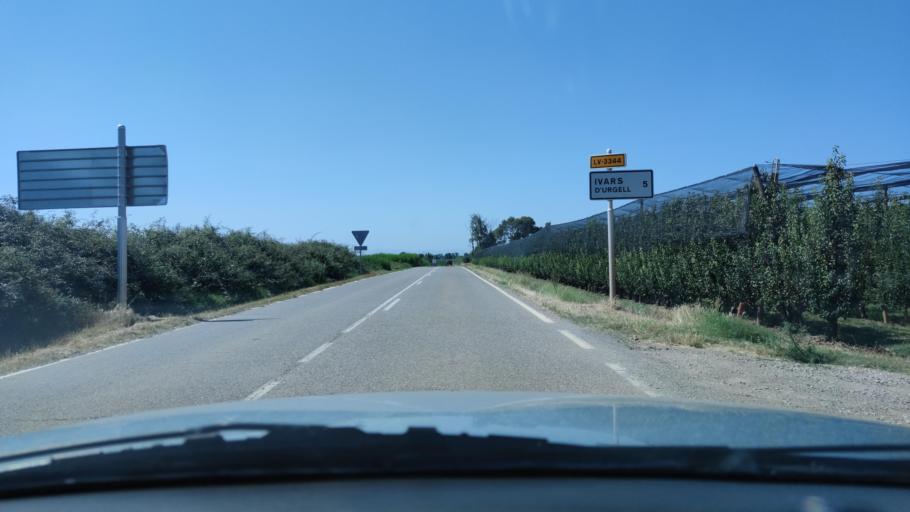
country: ES
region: Catalonia
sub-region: Provincia de Lleida
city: Penelles
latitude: 41.7282
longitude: 0.9827
